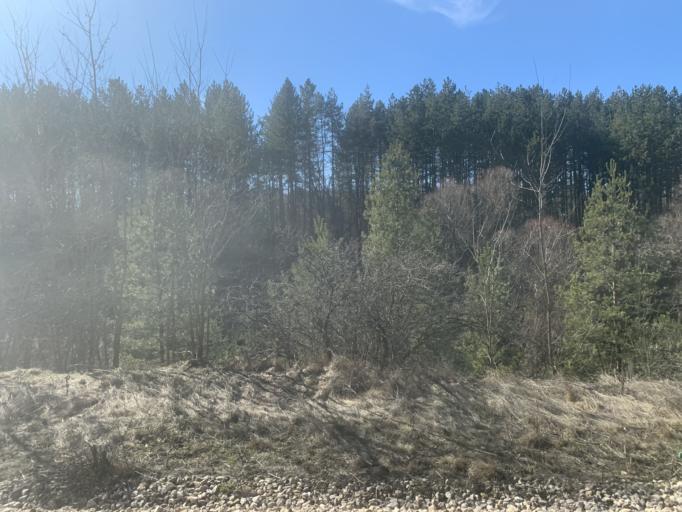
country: BG
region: Sofiya
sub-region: Obshtina Gorna Malina
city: Gorna Malina
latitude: 42.5645
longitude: 23.6844
